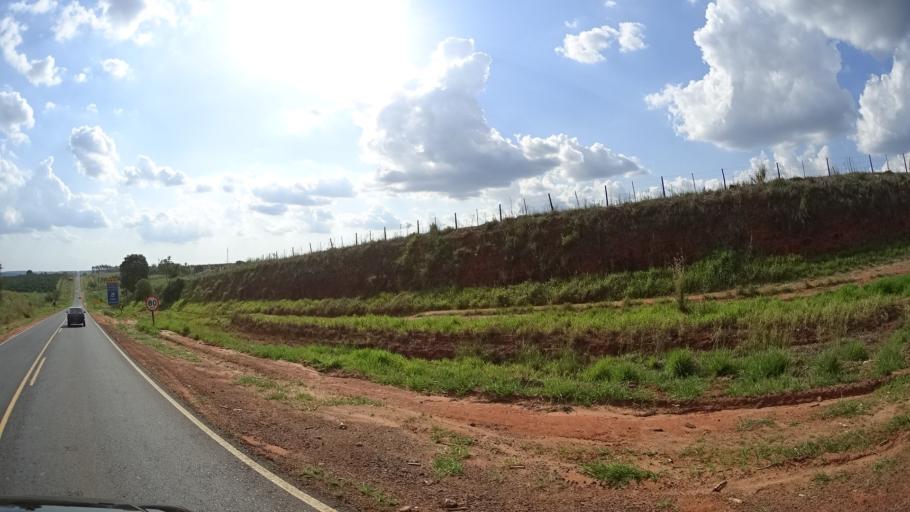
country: BR
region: Sao Paulo
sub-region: Urupes
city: Urupes
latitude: -21.1869
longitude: -49.2979
